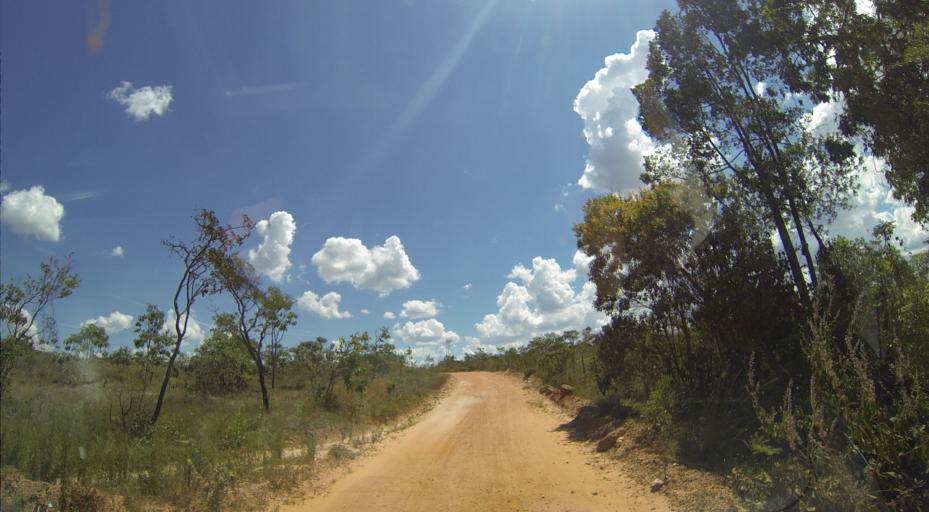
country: BR
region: Minas Gerais
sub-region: Serro
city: Serro
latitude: -18.4900
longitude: -43.4725
